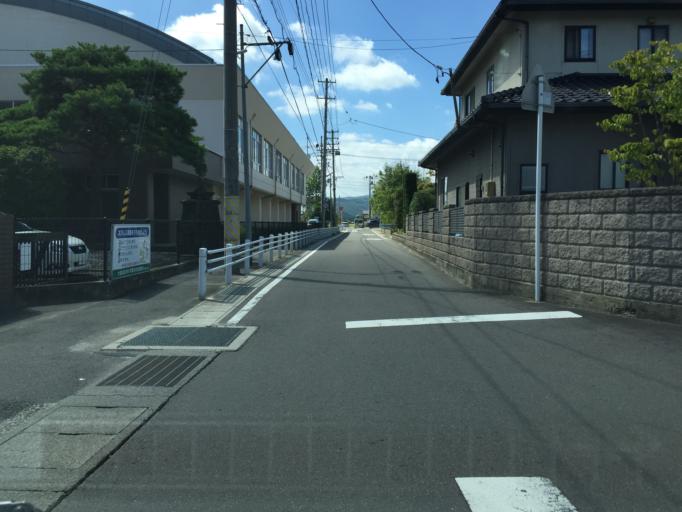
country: JP
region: Fukushima
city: Fukushima-shi
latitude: 37.7274
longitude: 140.4414
